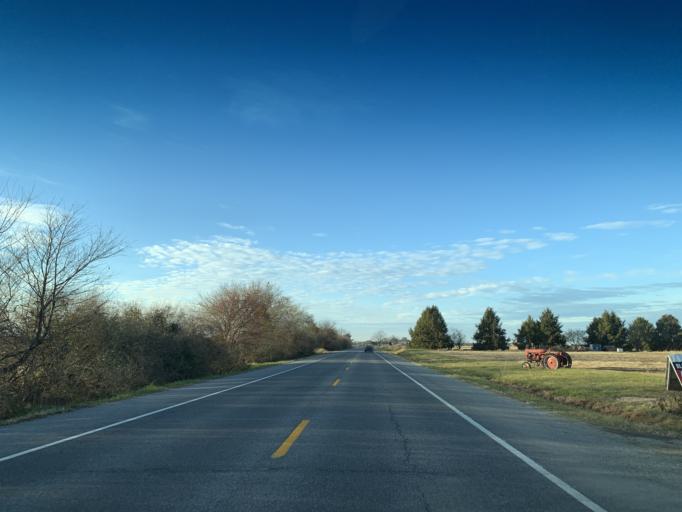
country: US
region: Maryland
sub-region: Kent County
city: Chestertown
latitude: 39.2538
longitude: -76.0789
